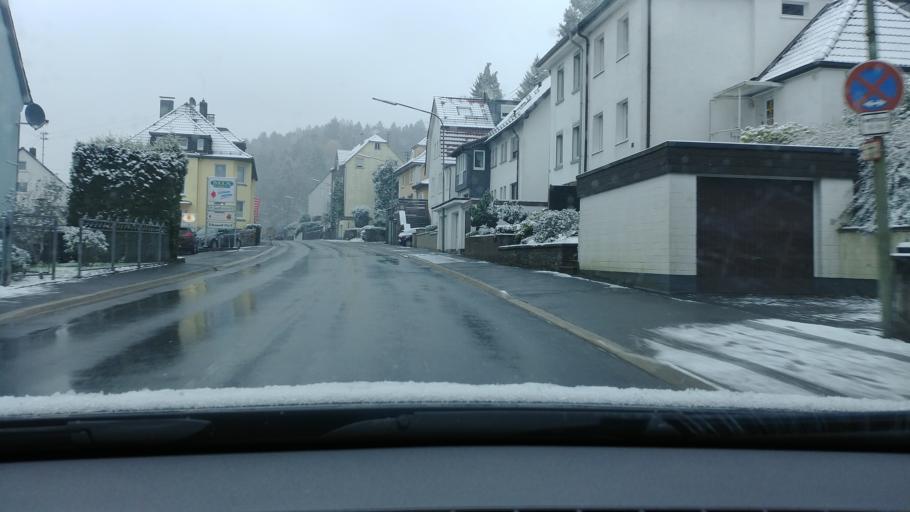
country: DE
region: North Rhine-Westphalia
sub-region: Regierungsbezirk Koln
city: Gummersbach
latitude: 51.0223
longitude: 7.5760
